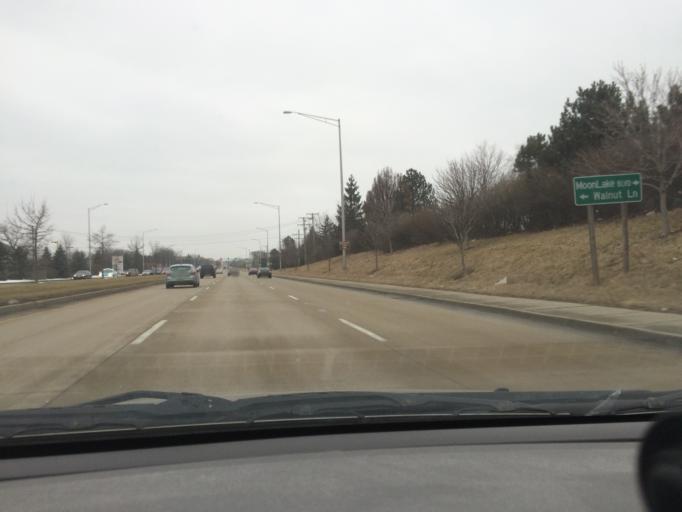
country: US
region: Illinois
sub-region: Cook County
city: Schaumburg
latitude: 42.0476
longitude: -88.1225
